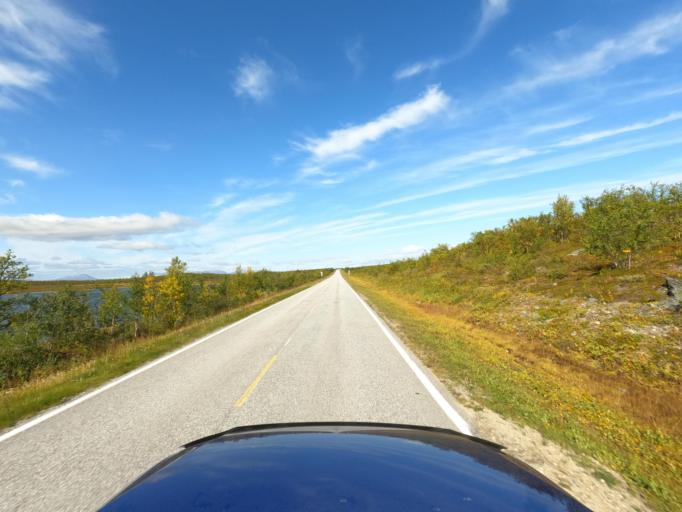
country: NO
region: Finnmark Fylke
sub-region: Karasjok
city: Karasjohka
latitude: 69.7038
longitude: 25.2514
